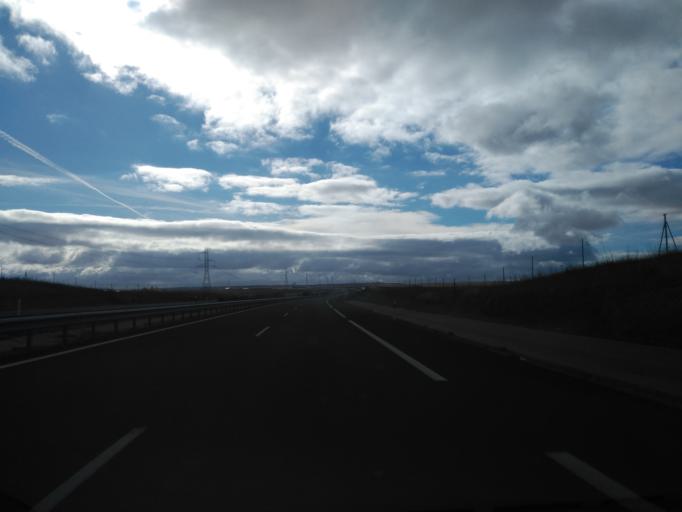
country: ES
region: Castille and Leon
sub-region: Provincia de Palencia
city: Abia de las Torres
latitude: 42.3837
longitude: -4.3860
